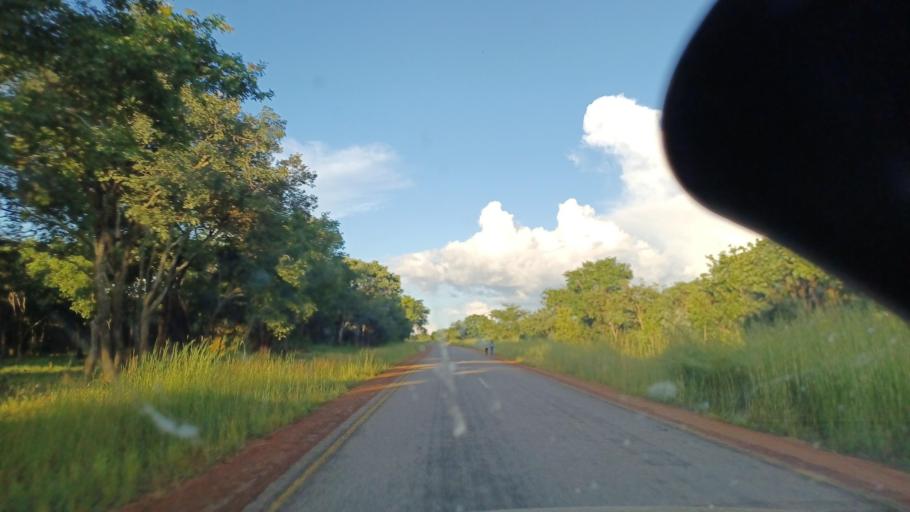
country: ZM
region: North-Western
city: Kalengwa
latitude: -13.1371
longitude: 25.1576
